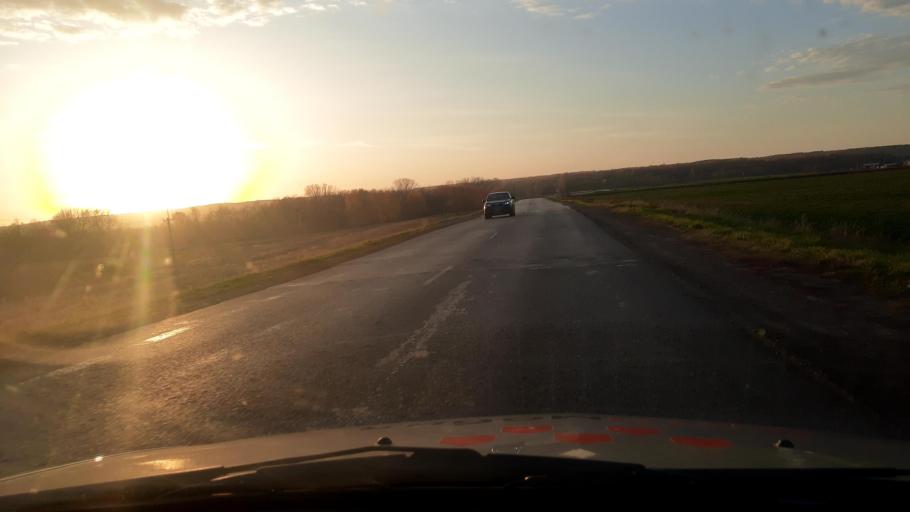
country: RU
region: Bashkortostan
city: Mikhaylovka
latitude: 54.8314
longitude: 55.9509
